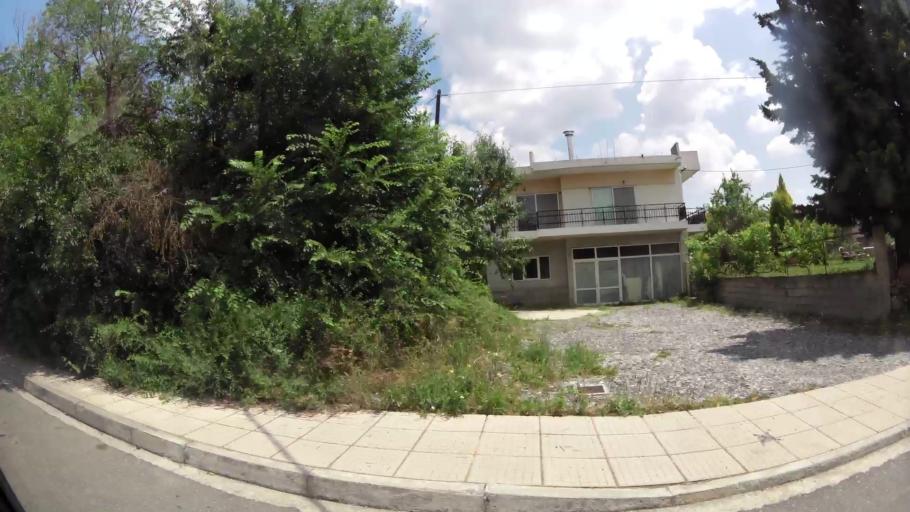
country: GR
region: West Macedonia
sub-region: Nomos Kozanis
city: Kozani
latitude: 40.2897
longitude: 21.7971
